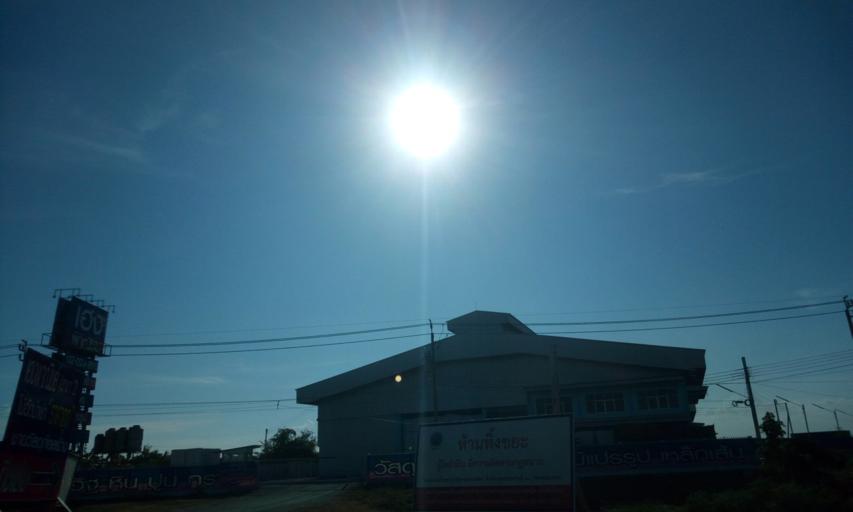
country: TH
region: Samut Prakan
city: Bang Bo District
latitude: 13.5403
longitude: 100.7505
